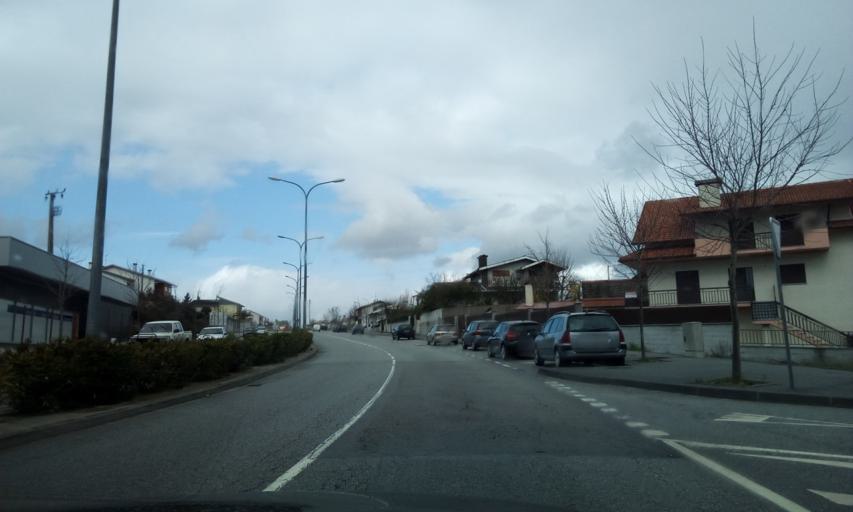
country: PT
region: Viseu
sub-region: Viseu
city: Viseu
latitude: 40.6217
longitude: -7.9181
